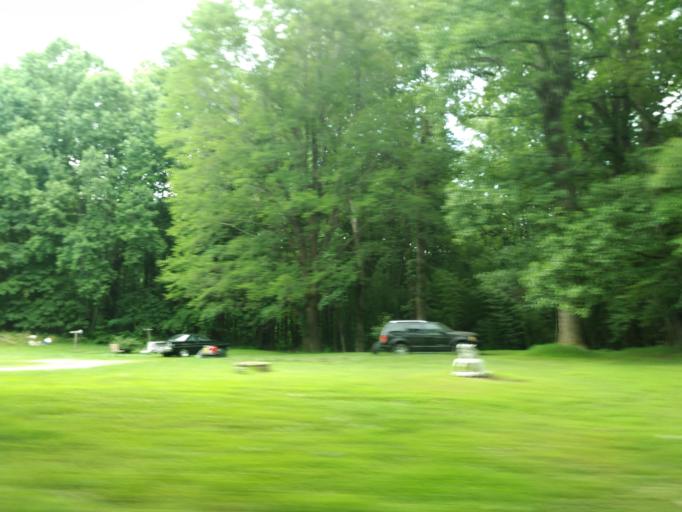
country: US
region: Maryland
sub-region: Anne Arundel County
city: Deale
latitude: 38.8238
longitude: -76.5823
